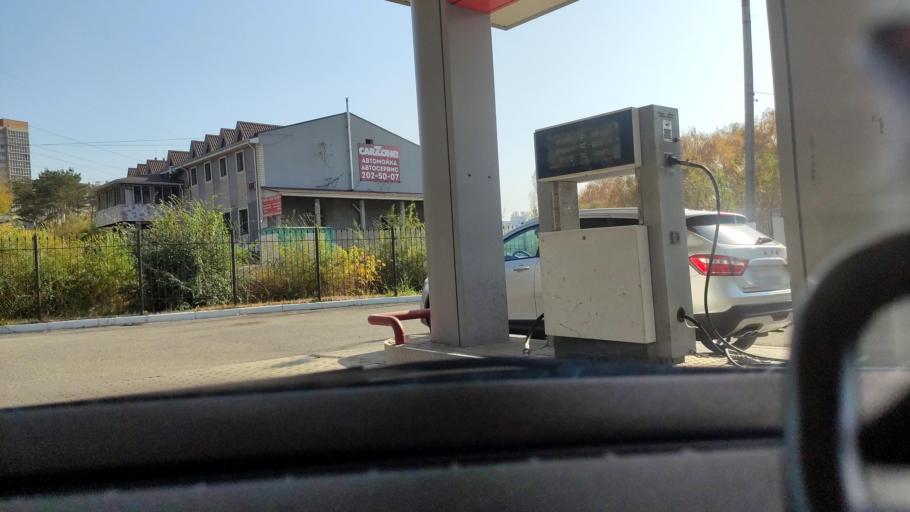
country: RU
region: Voronezj
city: Pridonskoy
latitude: 51.6465
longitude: 39.1196
